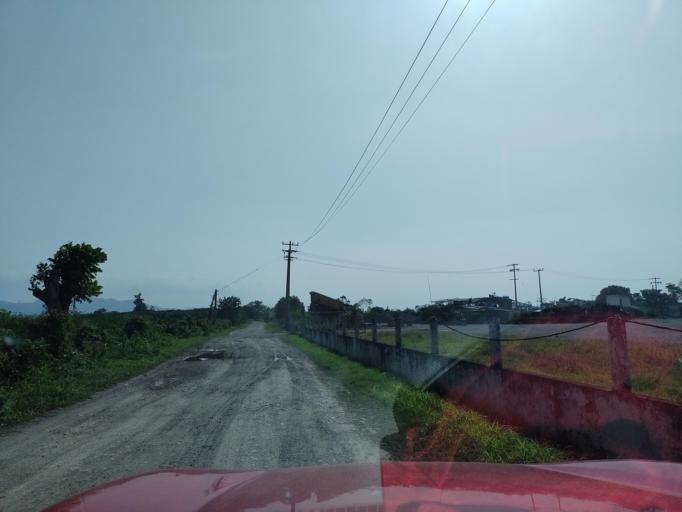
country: MX
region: Puebla
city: Espinal
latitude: 20.2723
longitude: -97.3294
